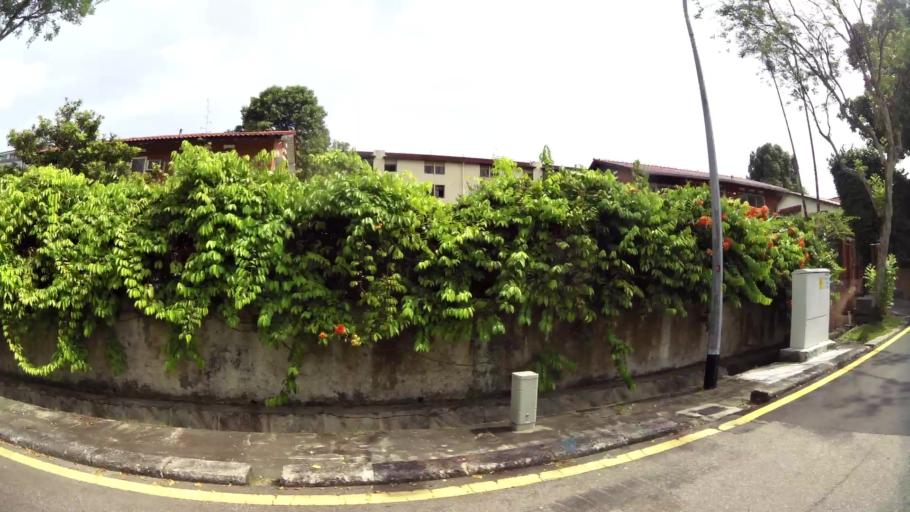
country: SG
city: Singapore
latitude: 1.3299
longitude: 103.7675
